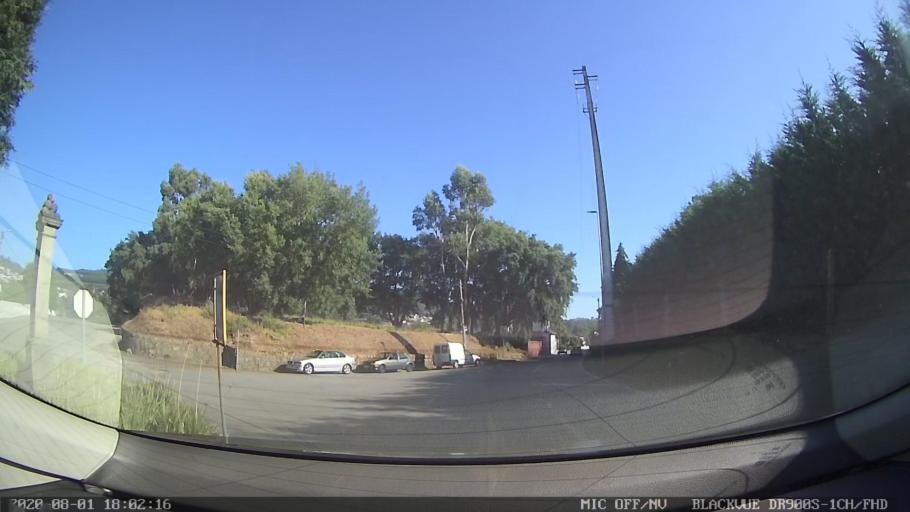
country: PT
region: Porto
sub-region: Santo Tirso
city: Santo Tirso
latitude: 41.3515
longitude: -8.4666
